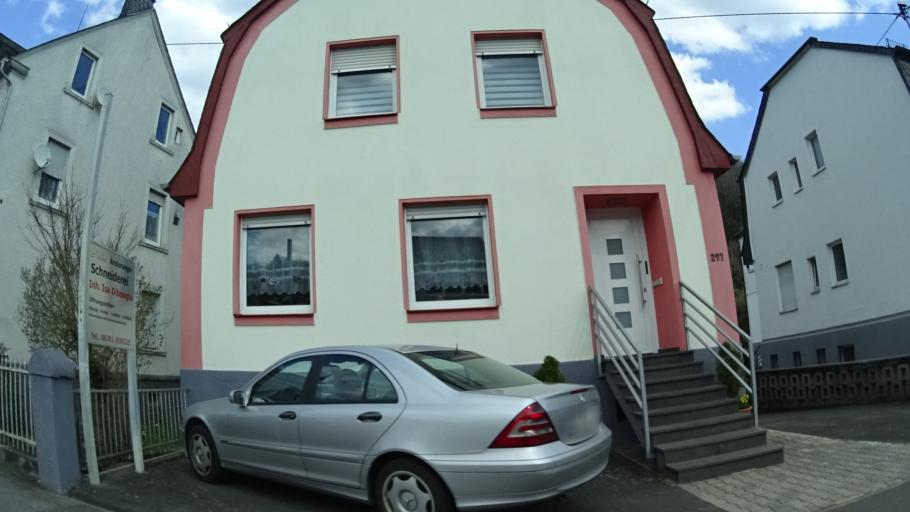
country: DE
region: Rheinland-Pfalz
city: Veitsrodt
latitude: 49.7430
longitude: 7.2778
